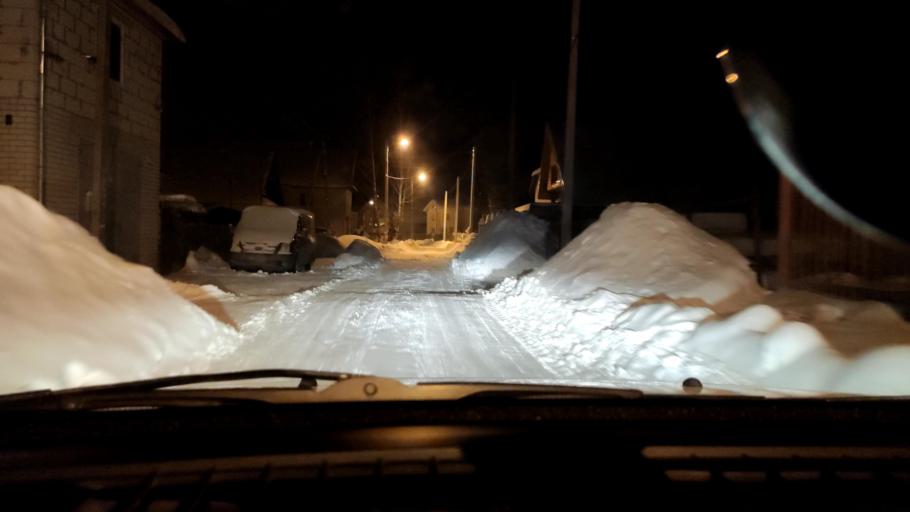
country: RU
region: Perm
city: Kondratovo
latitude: 58.0271
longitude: 55.9908
